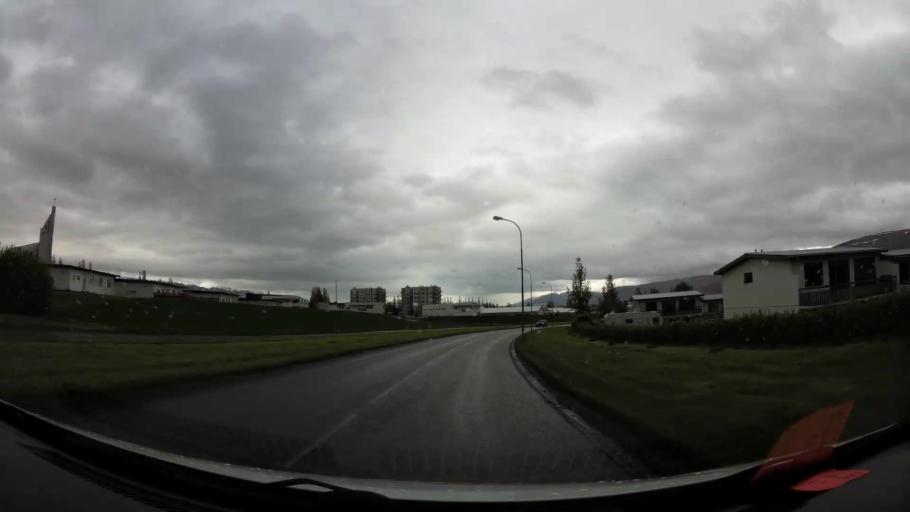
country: IS
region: Northeast
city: Akureyri
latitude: 65.6919
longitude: -18.1294
